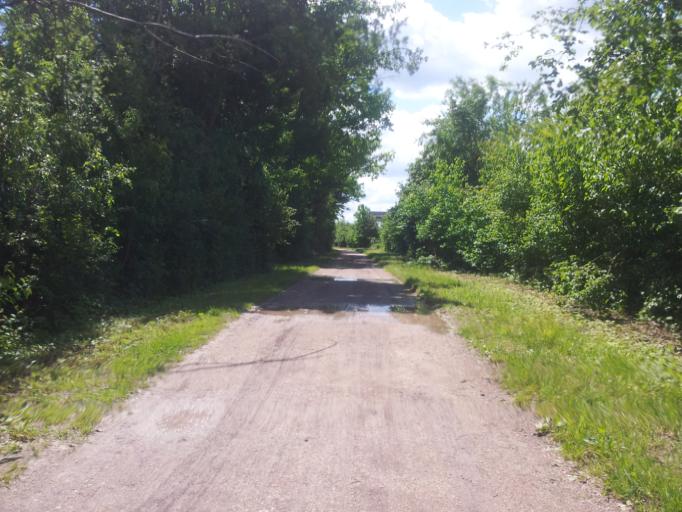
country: DE
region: Baden-Wuerttemberg
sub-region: Regierungsbezirk Stuttgart
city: Kongen
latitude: 48.6816
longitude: 9.3747
